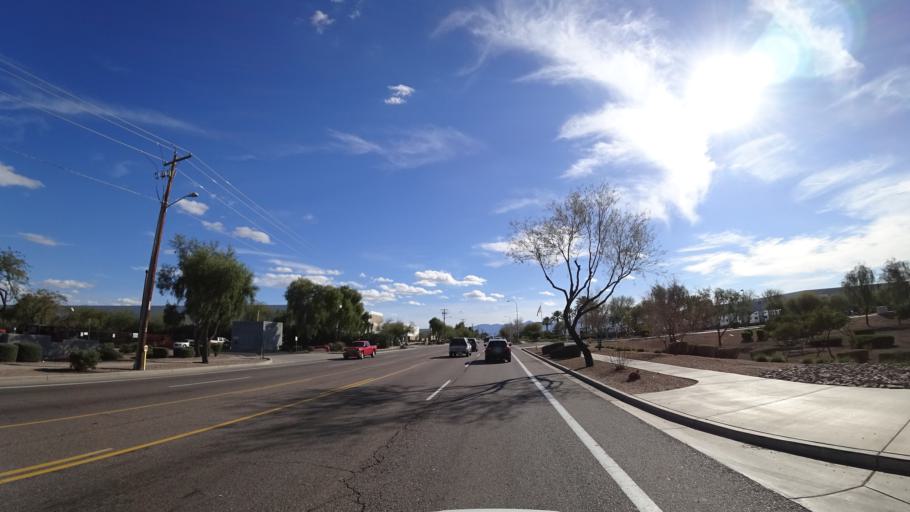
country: US
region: Arizona
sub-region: Maricopa County
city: Tolleson
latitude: 33.4561
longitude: -112.2211
